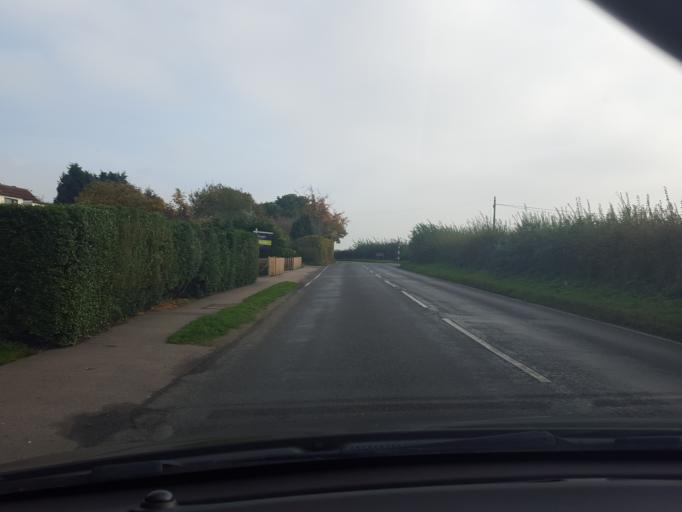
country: GB
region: England
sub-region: Essex
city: Mistley
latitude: 51.9401
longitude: 1.0943
